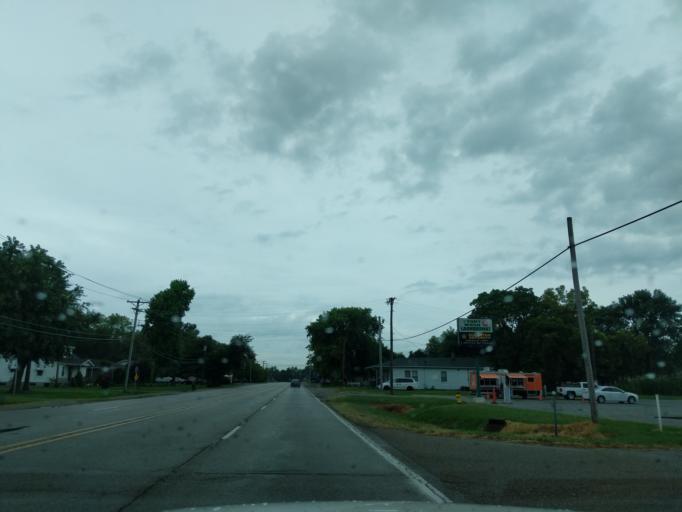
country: US
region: Illinois
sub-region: Saint Clair County
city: Fairmont City
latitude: 38.6594
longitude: -90.0862
